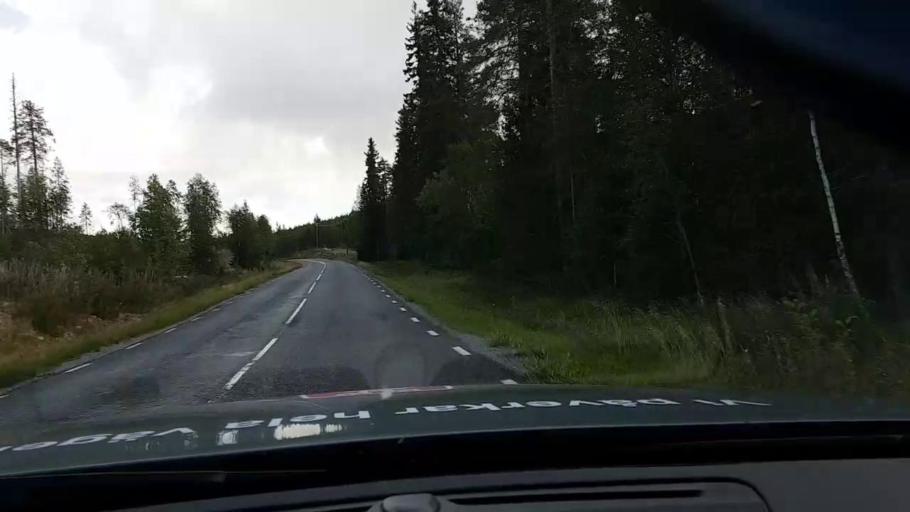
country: SE
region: Vaesterbotten
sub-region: Asele Kommun
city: Asele
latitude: 63.8317
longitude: 17.4522
